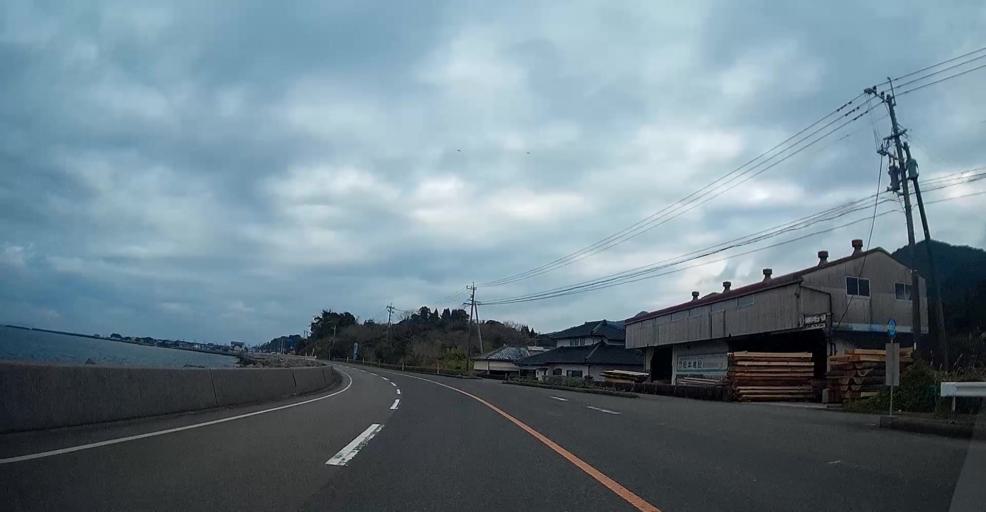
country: JP
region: Kumamoto
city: Hondo
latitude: 32.4675
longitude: 130.2465
